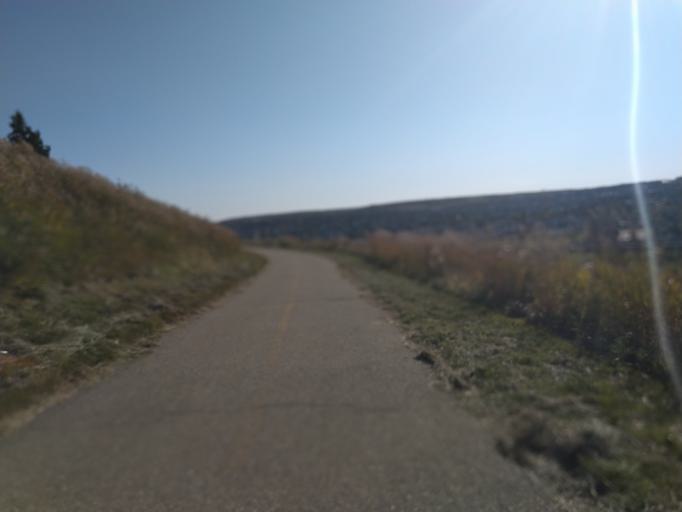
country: CA
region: Alberta
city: Calgary
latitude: 51.1568
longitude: -114.0962
